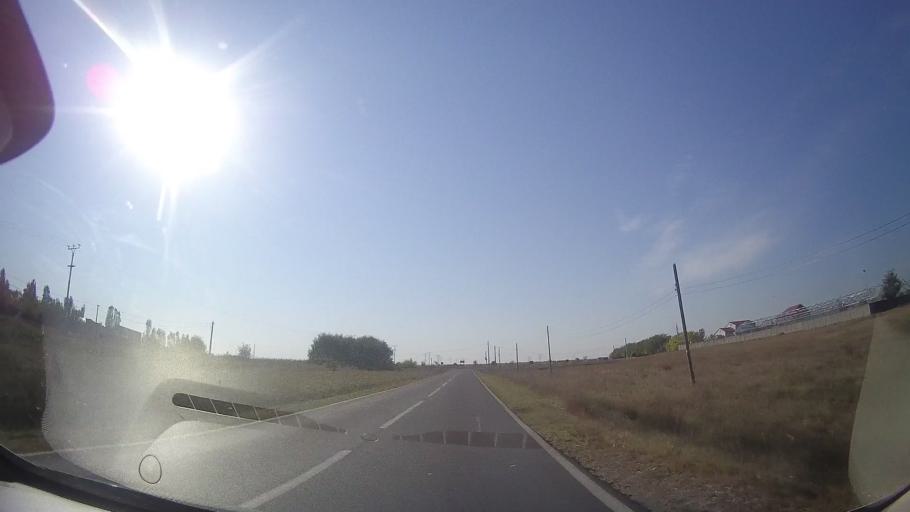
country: RO
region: Timis
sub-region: Oras Recas
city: Recas
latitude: 45.8091
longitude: 21.5289
